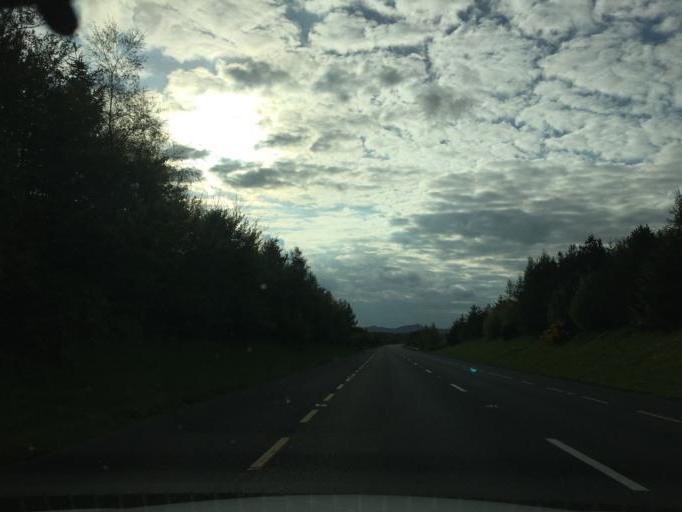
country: IE
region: Leinster
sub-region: Loch Garman
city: Enniscorthy
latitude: 52.3533
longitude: -6.6757
